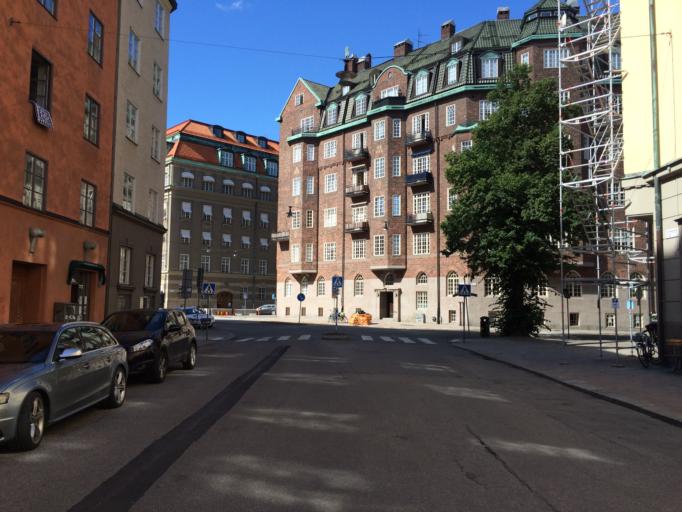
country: SE
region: Stockholm
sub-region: Stockholms Kommun
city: OEstermalm
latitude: 59.3393
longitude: 18.0885
